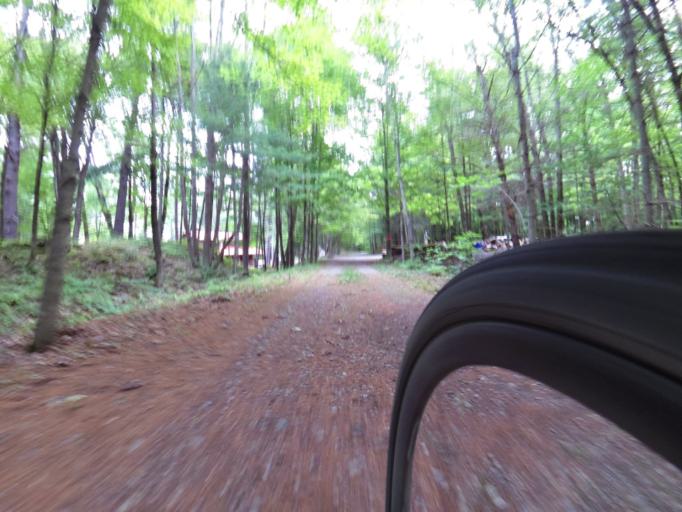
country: CA
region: Ontario
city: Gananoque
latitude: 44.5814
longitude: -76.3219
